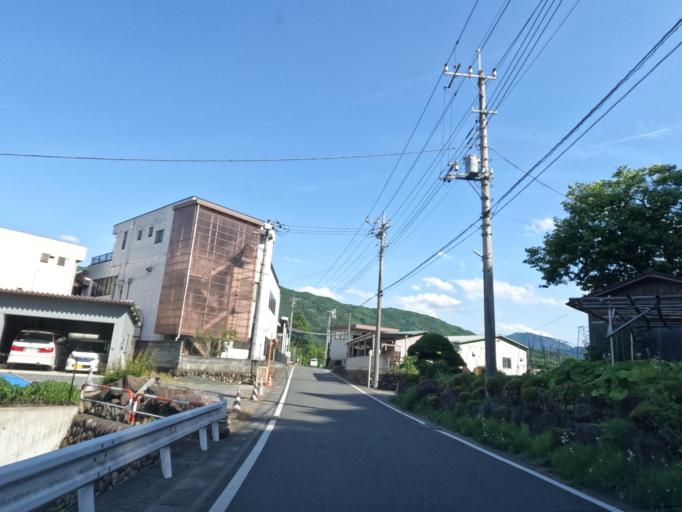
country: JP
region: Saitama
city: Chichibu
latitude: 36.0150
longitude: 139.1080
